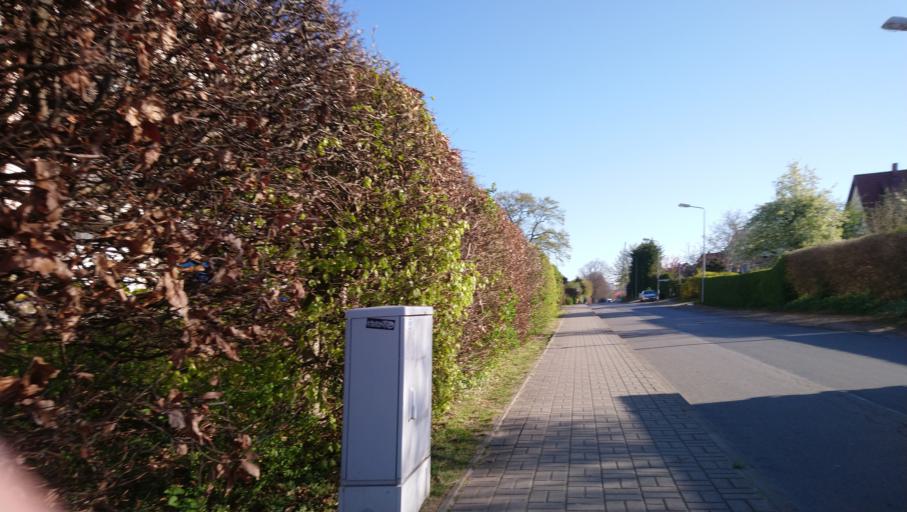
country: DE
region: Mecklenburg-Vorpommern
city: Rostock
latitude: 54.0655
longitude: 12.1319
